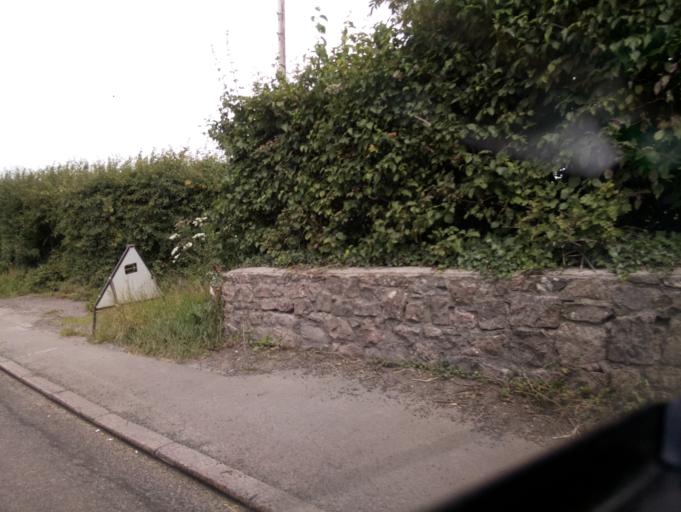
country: GB
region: England
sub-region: North Somerset
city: Yatton
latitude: 51.3971
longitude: -2.8343
